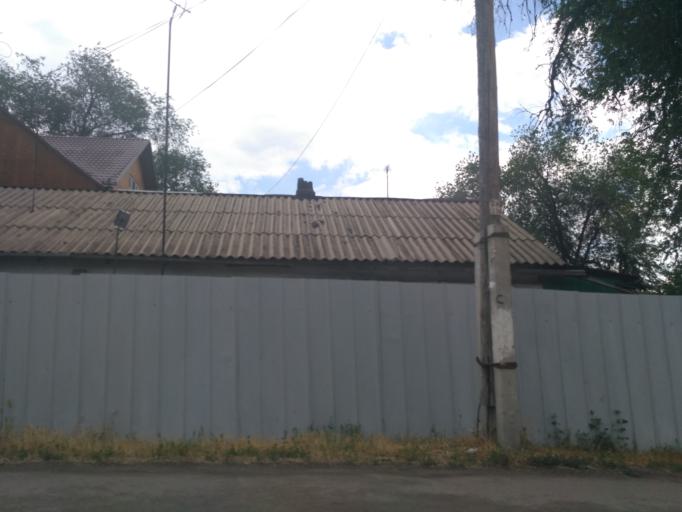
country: KZ
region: Almaty Oblysy
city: Burunday
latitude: 43.2014
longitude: 76.6344
